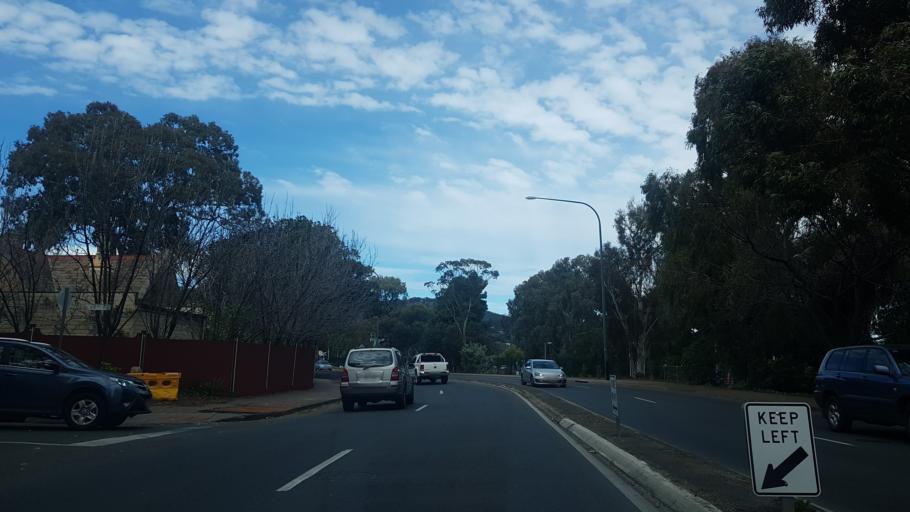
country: AU
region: South Australia
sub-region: Mitcham
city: Hawthorn
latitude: -34.9774
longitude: 138.6095
